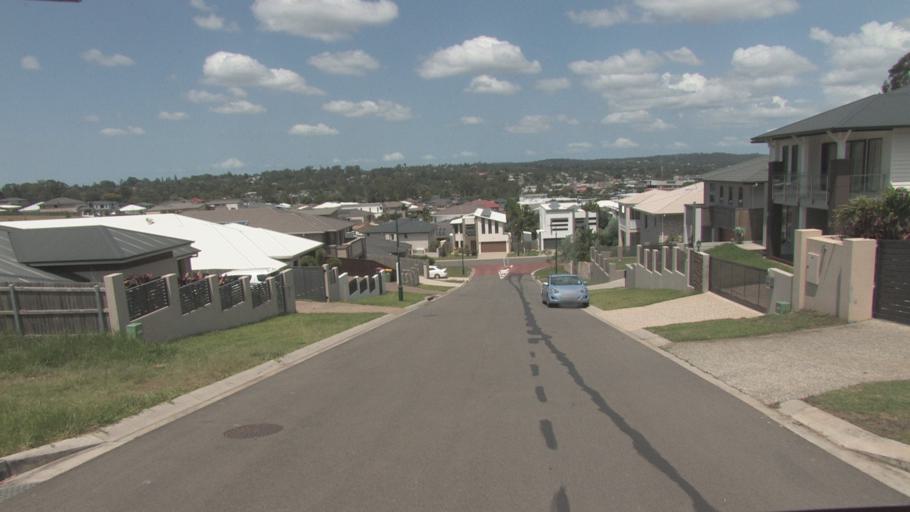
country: AU
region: Queensland
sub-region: Logan
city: Rochedale South
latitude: -27.6046
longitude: 153.1051
